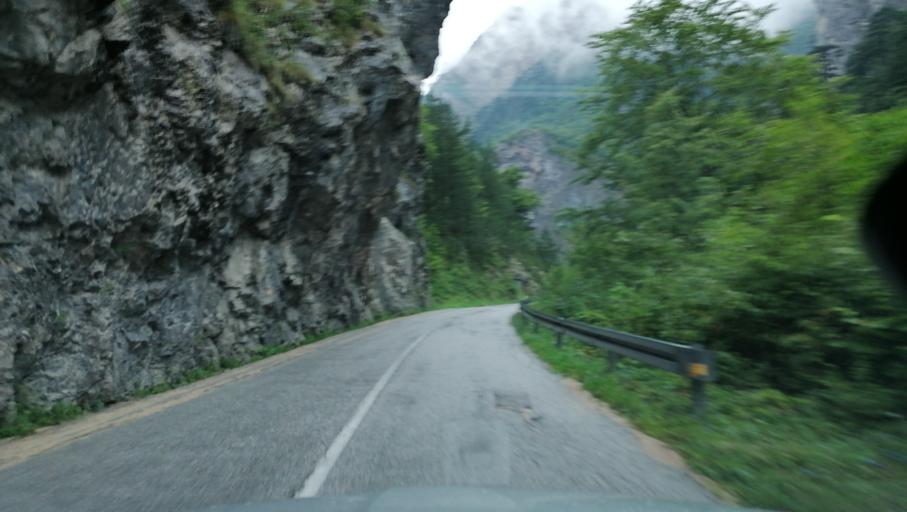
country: BA
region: Republika Srpska
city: Gacko
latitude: 43.3147
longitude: 18.6631
